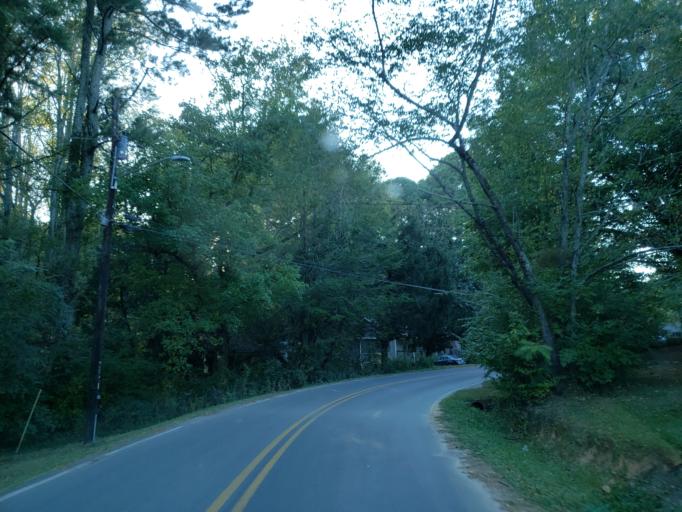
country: US
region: Georgia
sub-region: Pickens County
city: Jasper
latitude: 34.4615
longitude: -84.4240
